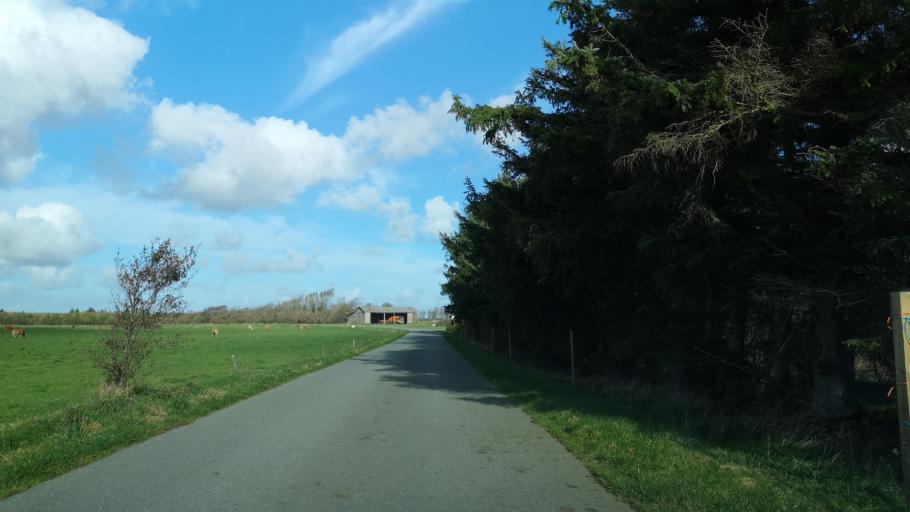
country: DK
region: South Denmark
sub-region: Varde Kommune
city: Oksbol
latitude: 55.7167
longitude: 8.2855
